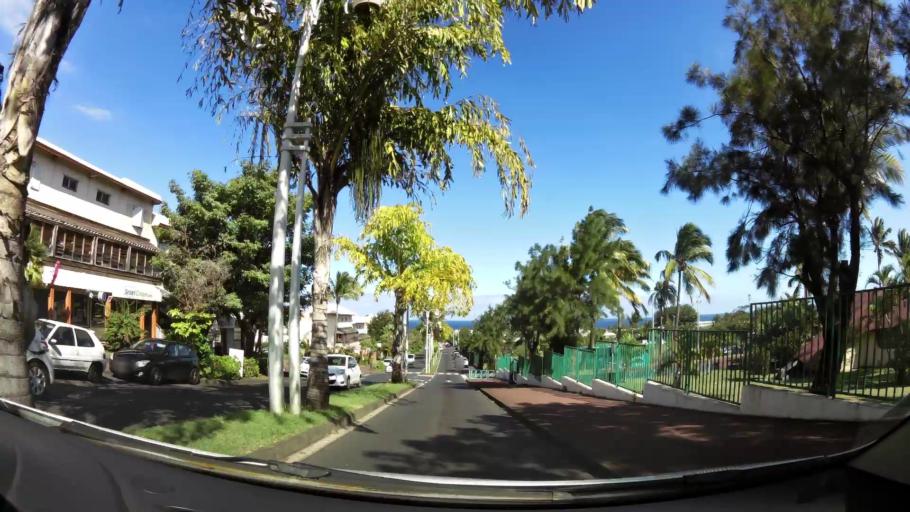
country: RE
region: Reunion
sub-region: Reunion
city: Saint-Pierre
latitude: -21.3316
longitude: 55.4720
